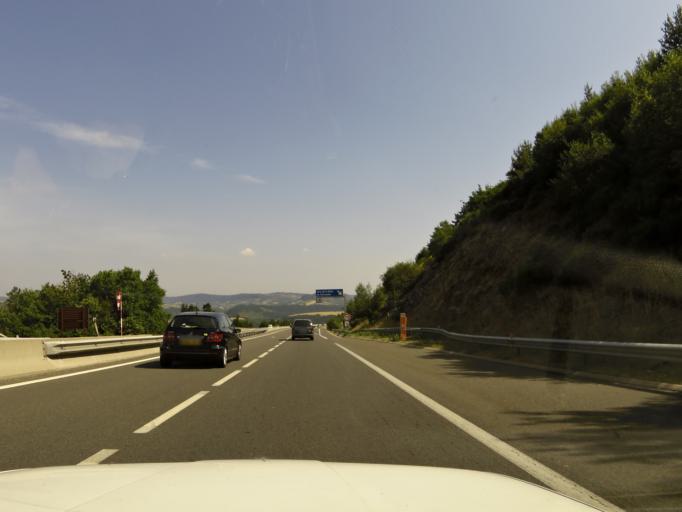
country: FR
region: Languedoc-Roussillon
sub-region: Departement de la Lozere
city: Marvejols
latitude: 44.5708
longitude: 3.2499
